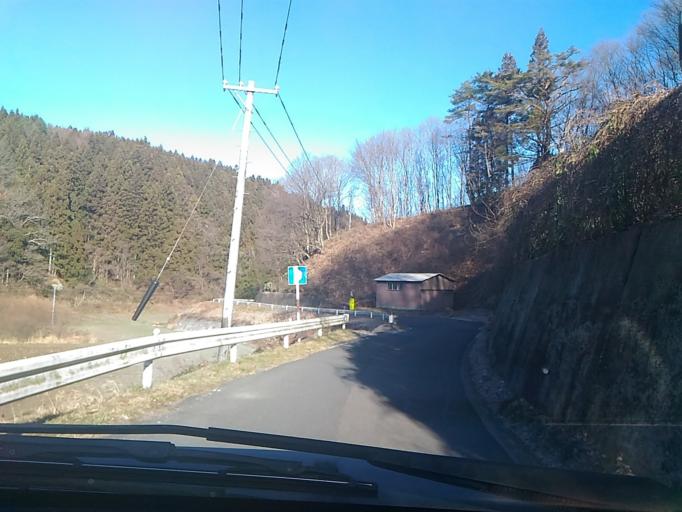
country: JP
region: Fukushima
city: Ishikawa
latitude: 37.0105
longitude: 140.5347
